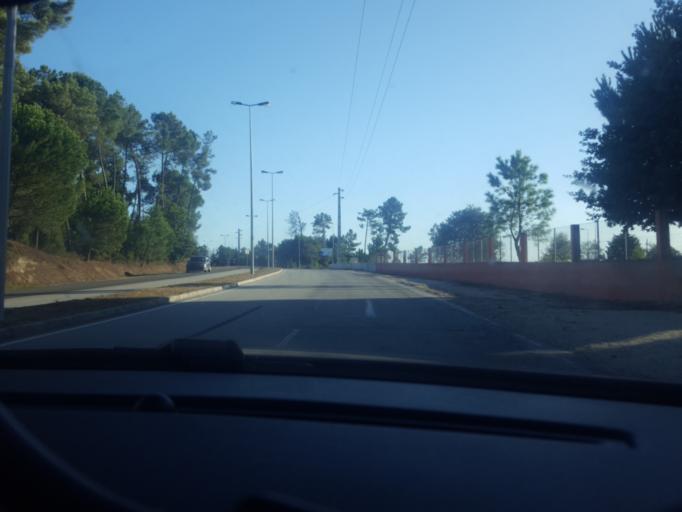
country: PT
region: Viseu
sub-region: Nelas
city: Nelas
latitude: 40.5297
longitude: -7.8661
